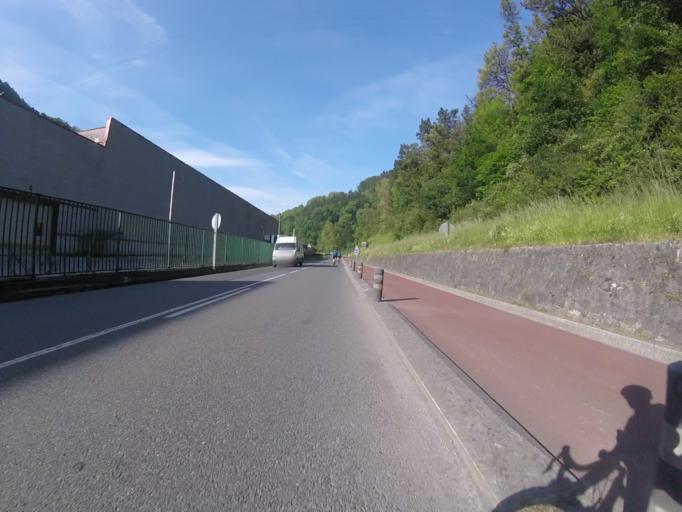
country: ES
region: Basque Country
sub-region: Provincia de Guipuzcoa
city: Isasondo
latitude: 43.0754
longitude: -2.1610
